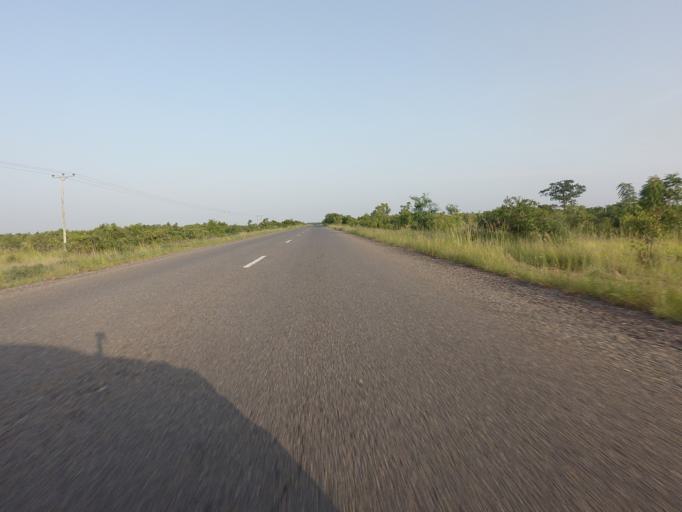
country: GH
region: Volta
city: Anloga
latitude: 5.9620
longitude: 0.6651
